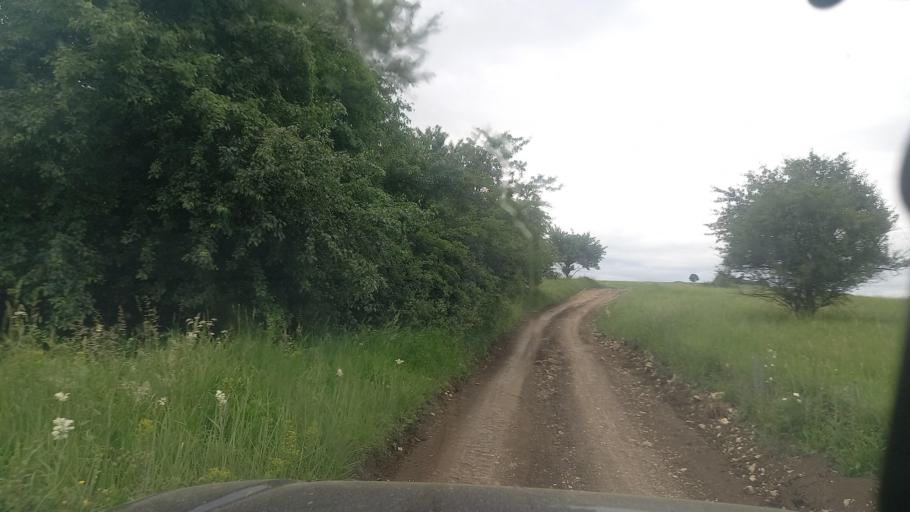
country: RU
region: Krasnodarskiy
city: Peredovaya
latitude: 44.0738
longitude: 41.3645
